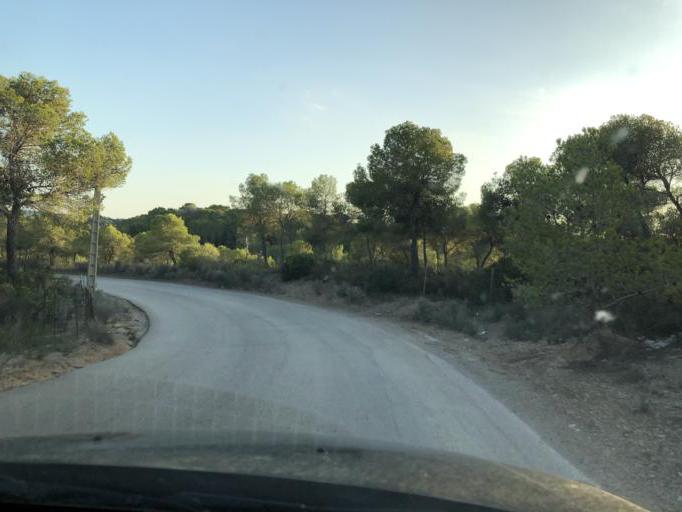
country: ES
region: Balearic Islands
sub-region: Illes Balears
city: Santa Ponsa
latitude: 39.5338
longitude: 2.4801
